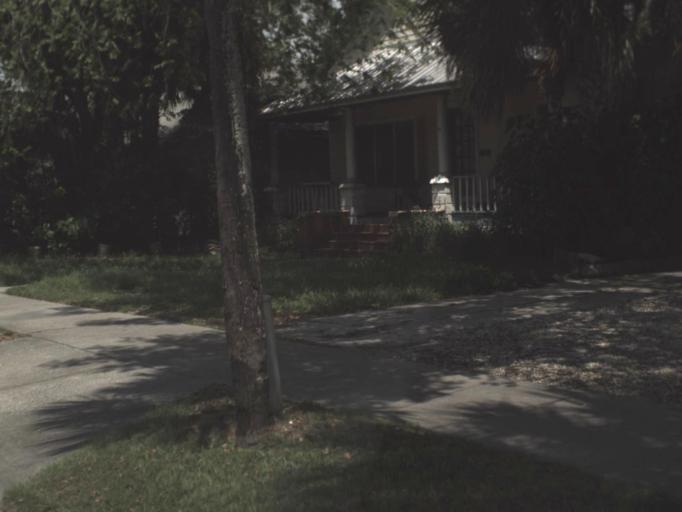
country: US
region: Florida
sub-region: Saint Johns County
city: Saint Augustine
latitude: 29.8915
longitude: -81.3195
